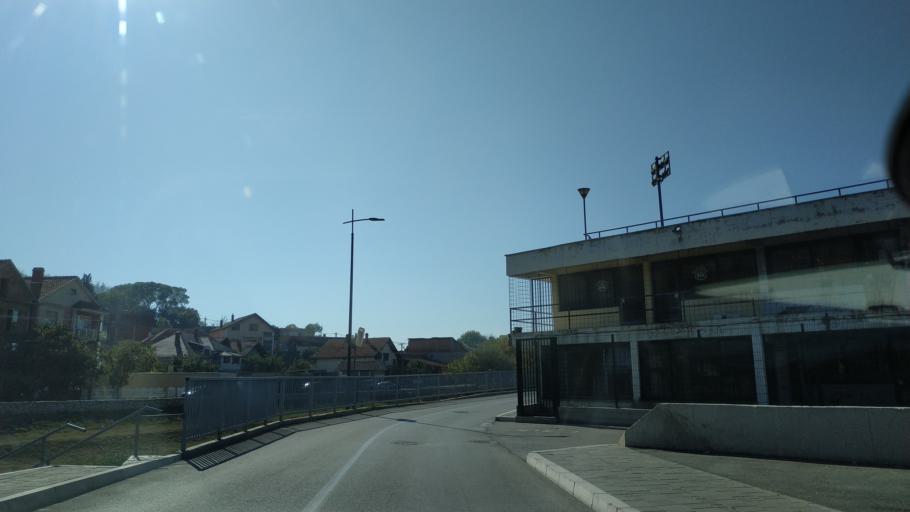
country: RS
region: Central Serbia
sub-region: Nisavski Okrug
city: Aleksinac
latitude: 43.5376
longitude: 21.7123
